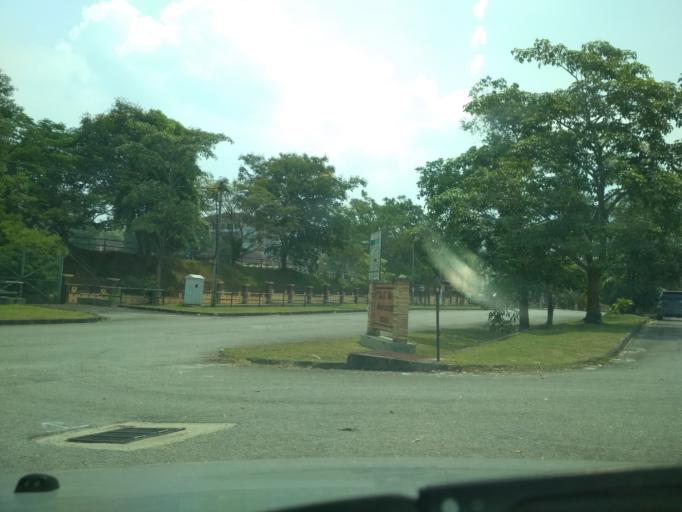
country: MY
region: Kedah
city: Kulim
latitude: 5.3584
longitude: 100.5357
